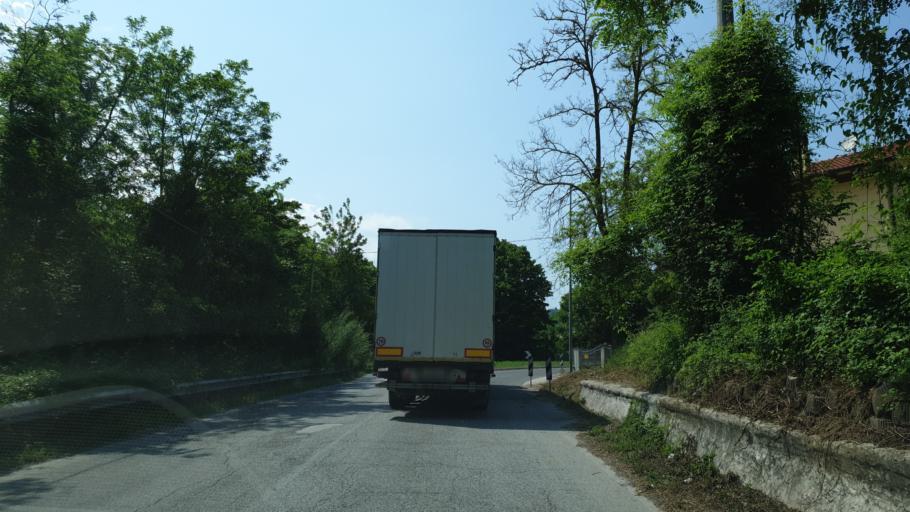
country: SM
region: Acquaviva
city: Acquaviva
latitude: 43.9591
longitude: 12.4026
